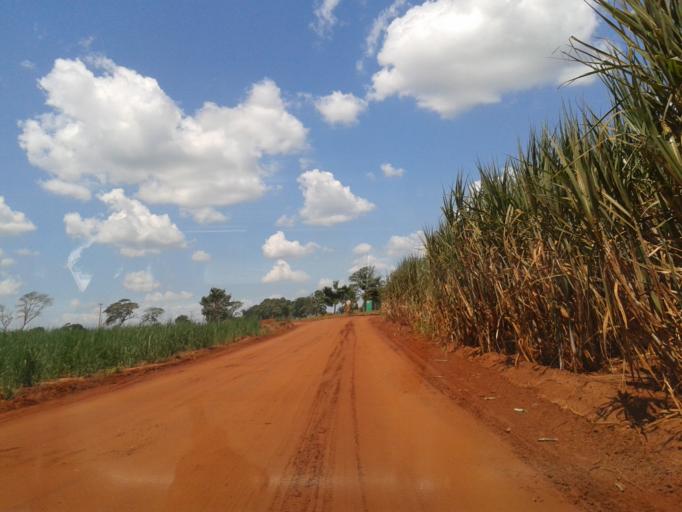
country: BR
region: Minas Gerais
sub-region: Ituiutaba
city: Ituiutaba
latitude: -18.9907
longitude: -49.6579
